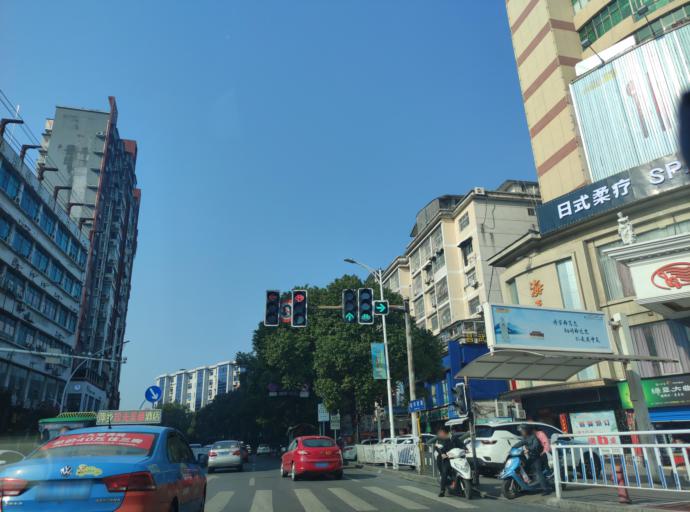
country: CN
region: Jiangxi Sheng
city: Pingxiang
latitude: 27.6338
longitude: 113.8428
